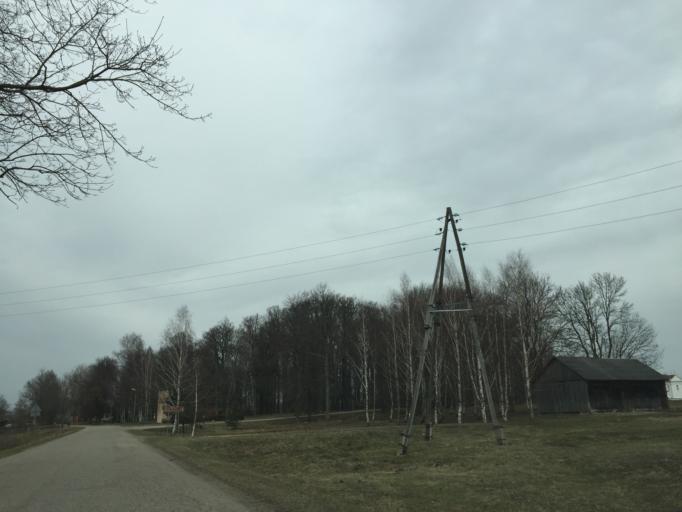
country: LV
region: Ilukste
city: Ilukste
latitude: 56.0538
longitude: 26.2831
